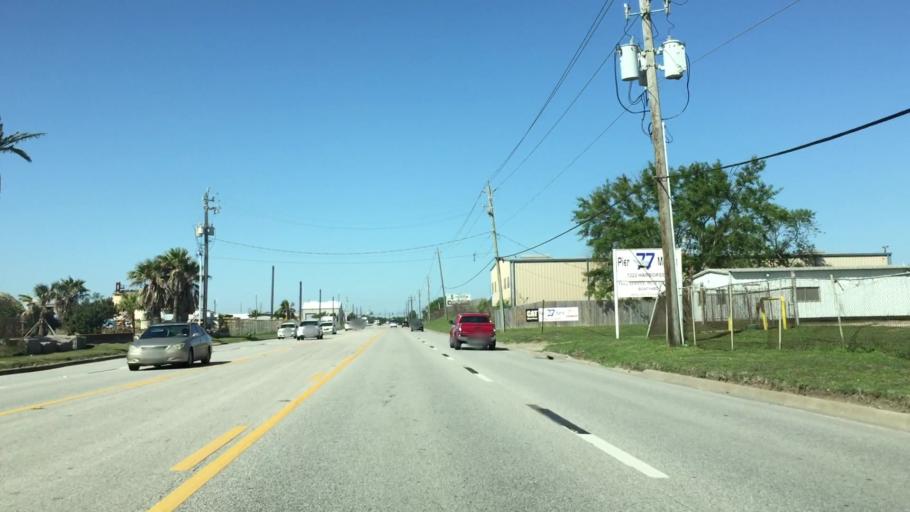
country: US
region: Texas
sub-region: Galveston County
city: Galveston
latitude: 29.2942
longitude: -94.8551
